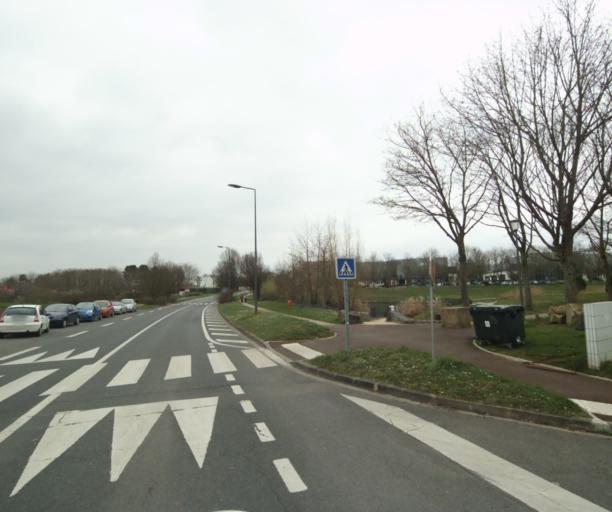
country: FR
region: Ile-de-France
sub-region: Departement du Val-d'Oise
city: Vaureal
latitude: 49.0554
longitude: 2.0376
